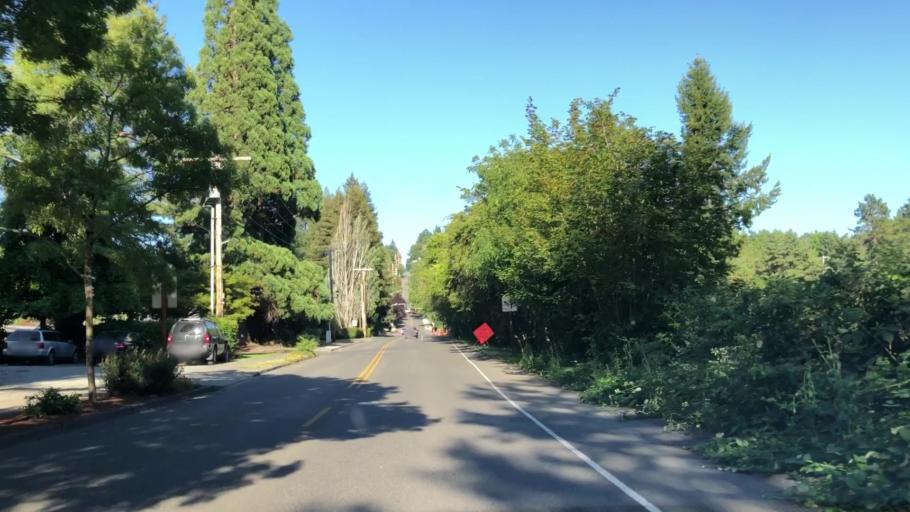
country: US
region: Washington
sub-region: King County
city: Medina
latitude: 47.6320
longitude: -122.2305
